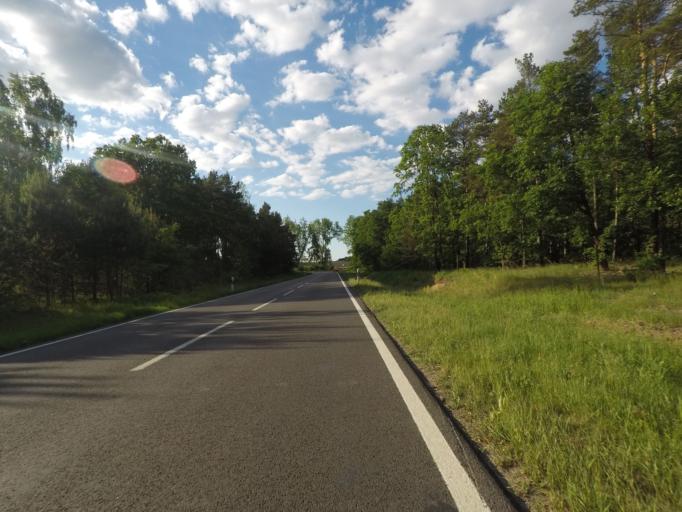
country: DE
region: Brandenburg
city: Britz
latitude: 52.8703
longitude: 13.8082
